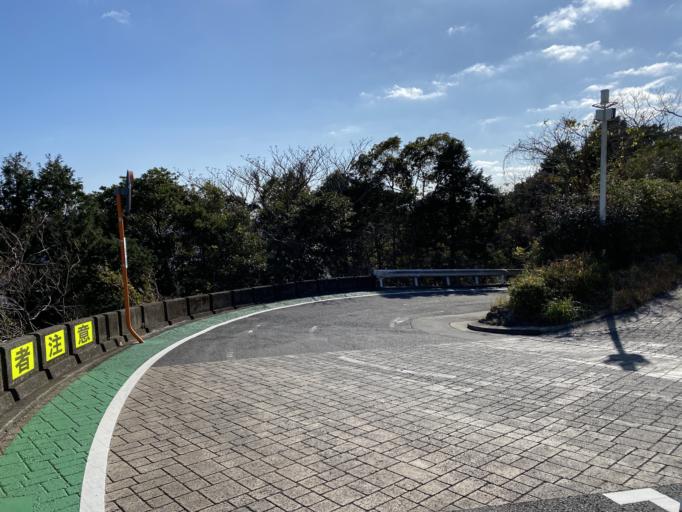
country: JP
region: Nagasaki
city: Nagasaki-shi
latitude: 32.7542
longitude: 129.8495
